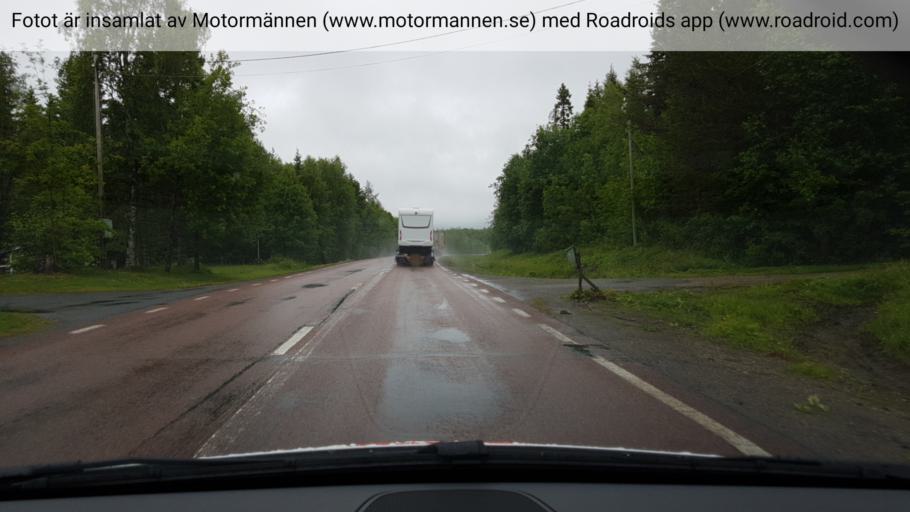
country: SE
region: Jaemtland
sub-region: Stroemsunds Kommun
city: Stroemsund
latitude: 63.8731
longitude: 15.5864
